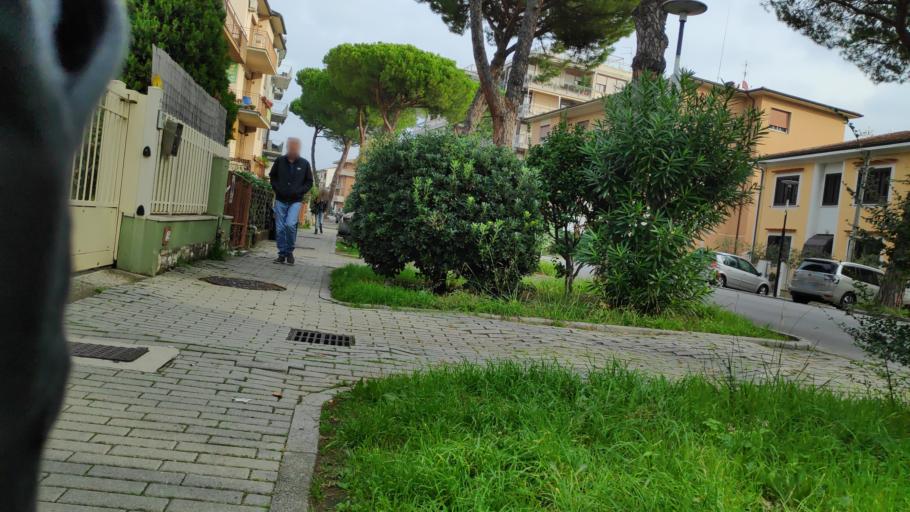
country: IT
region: Tuscany
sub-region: Province of Pisa
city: Pisa
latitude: 43.7013
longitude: 10.4002
